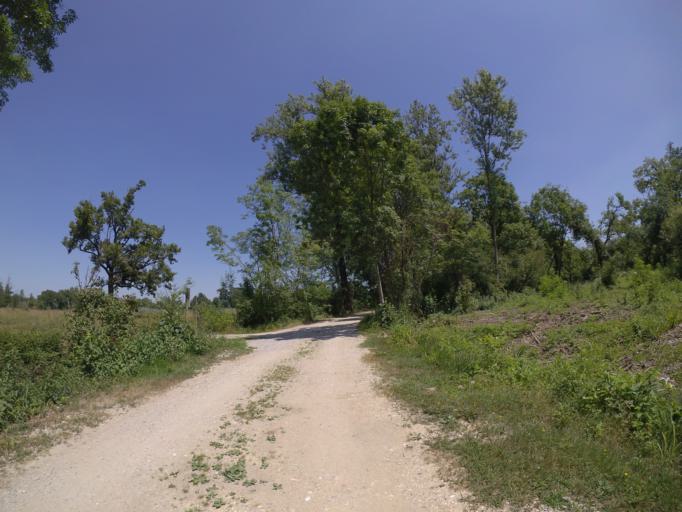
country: IT
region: Friuli Venezia Giulia
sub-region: Provincia di Udine
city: Bertiolo
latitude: 45.9153
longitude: 13.0772
